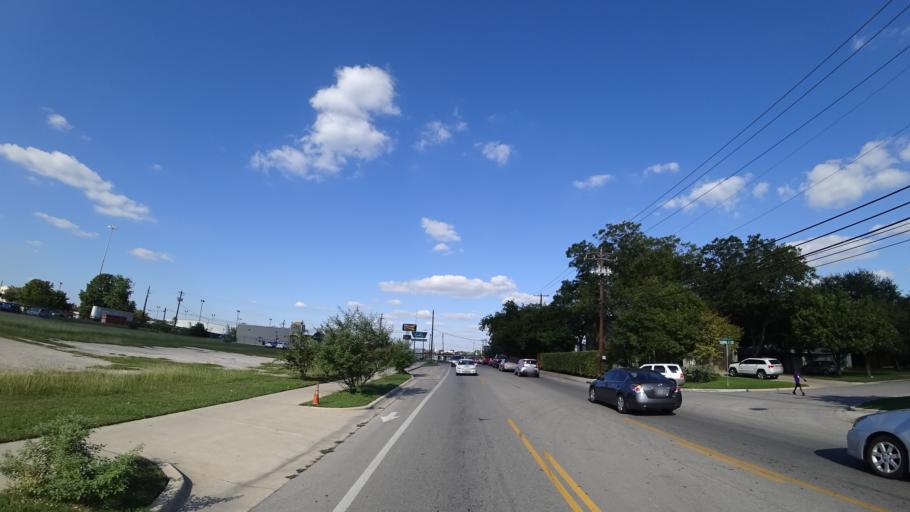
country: US
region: Texas
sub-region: Travis County
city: Austin
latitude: 30.3193
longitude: -97.6975
